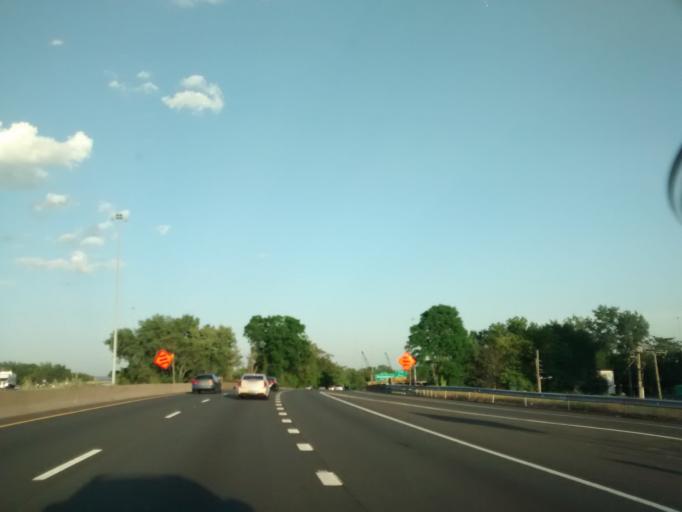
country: US
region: Connecticut
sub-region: Hartford County
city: Hartford
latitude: 41.7688
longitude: -72.6600
